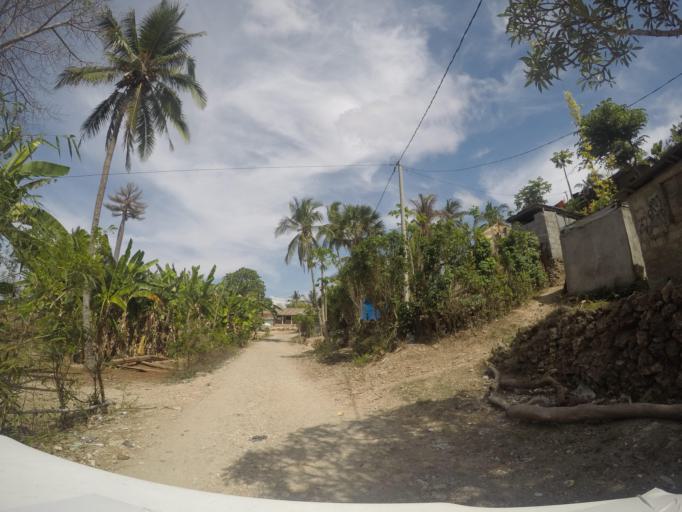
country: TL
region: Baucau
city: Baucau
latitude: -8.4680
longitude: 126.4617
